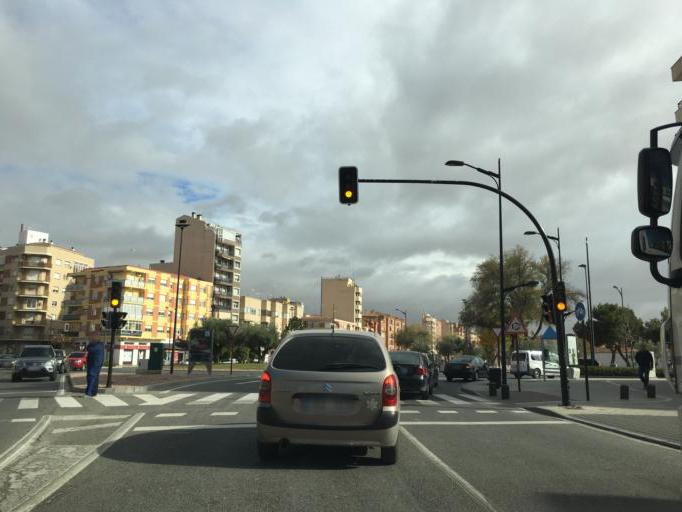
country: ES
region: Castille-La Mancha
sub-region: Provincia de Albacete
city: Albacete
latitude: 38.9984
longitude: -1.8722
